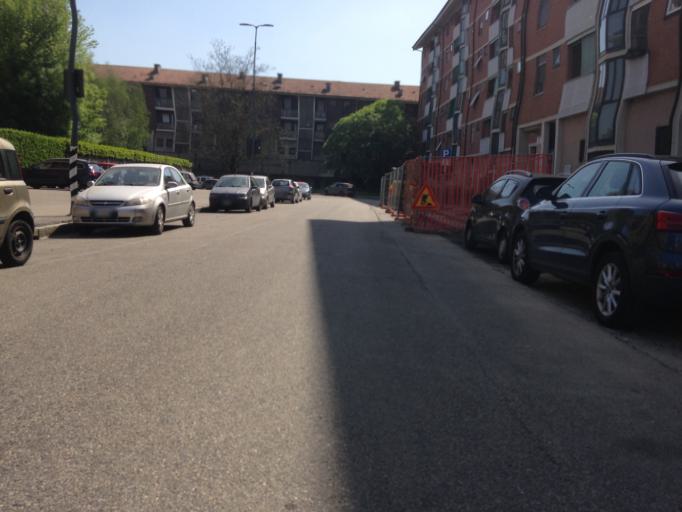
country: IT
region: Lombardy
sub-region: Citta metropolitana di Milano
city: Milano
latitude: 45.4285
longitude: 9.1755
